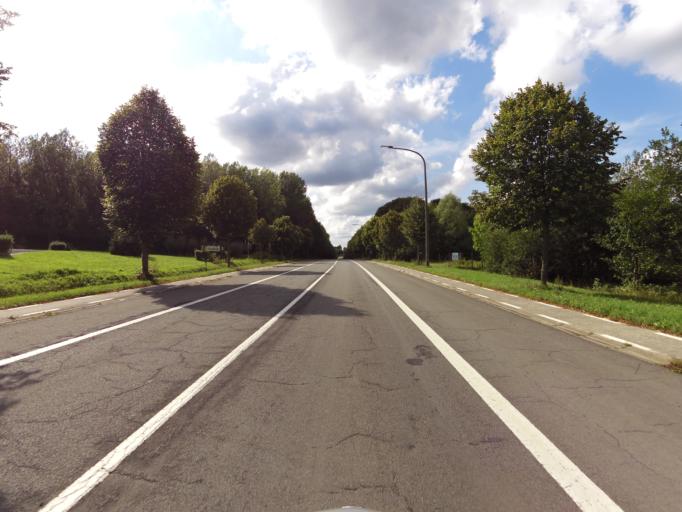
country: BE
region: Flanders
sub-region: Provincie Oost-Vlaanderen
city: Ronse
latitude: 50.7660
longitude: 3.5436
